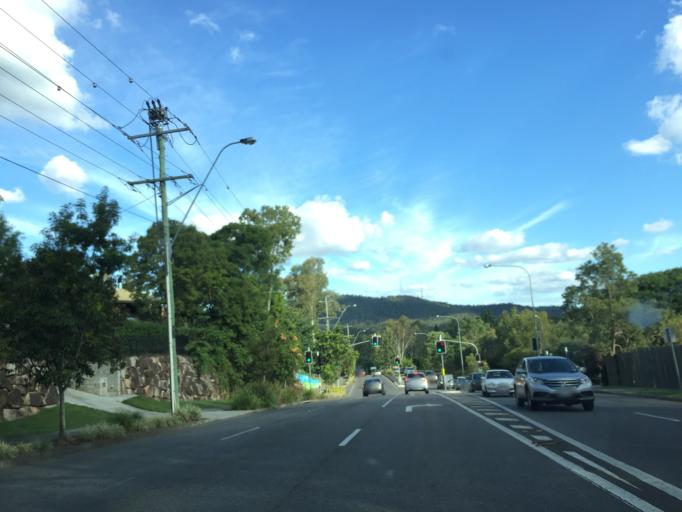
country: AU
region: Queensland
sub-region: Moreton Bay
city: Ferny Hills
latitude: -27.4361
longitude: 152.9434
